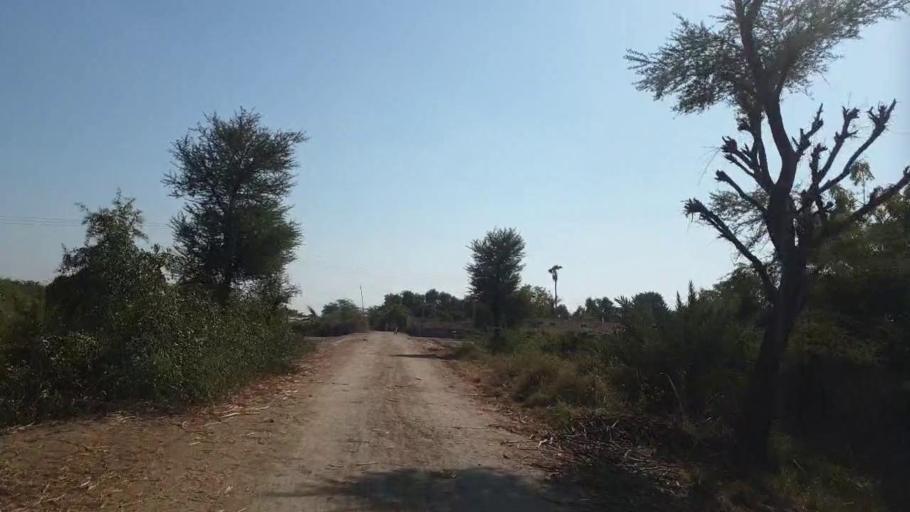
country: PK
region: Sindh
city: Mirpur Khas
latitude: 25.6445
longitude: 69.0227
